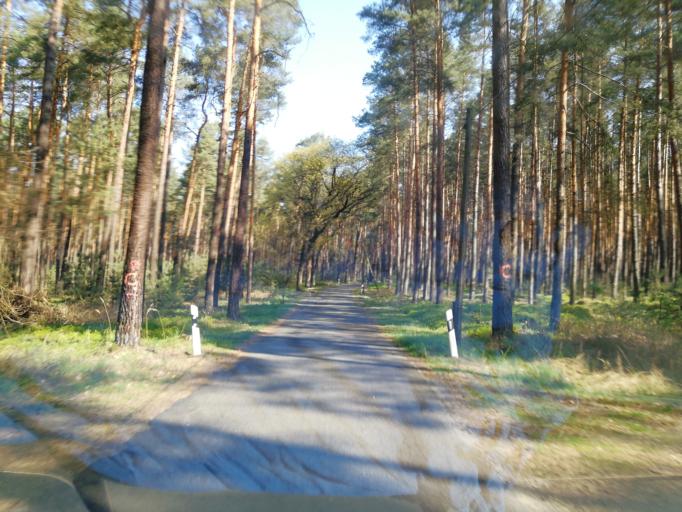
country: DE
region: Brandenburg
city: Bronkow
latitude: 51.6837
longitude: 13.8645
